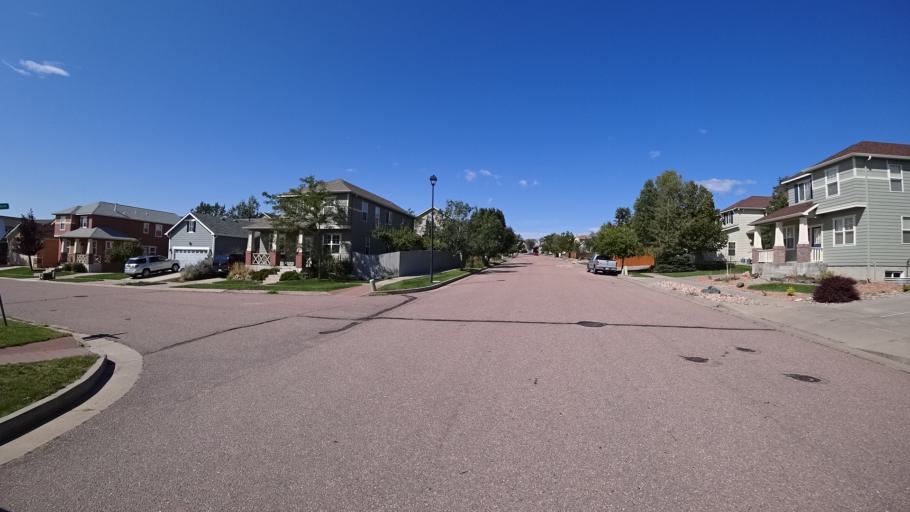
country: US
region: Colorado
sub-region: El Paso County
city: Cimarron Hills
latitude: 38.9201
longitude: -104.7019
